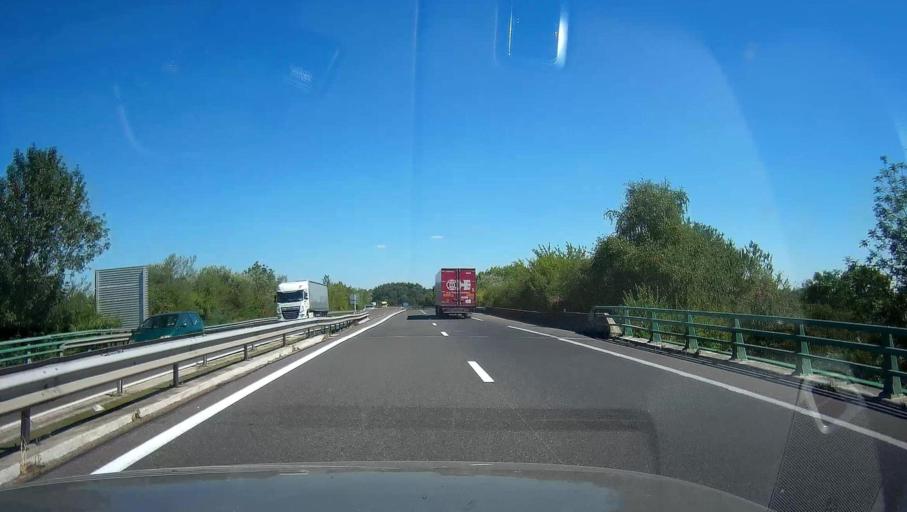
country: FR
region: Champagne-Ardenne
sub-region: Departement de la Marne
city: Fagnieres
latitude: 48.9834
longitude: 4.2919
